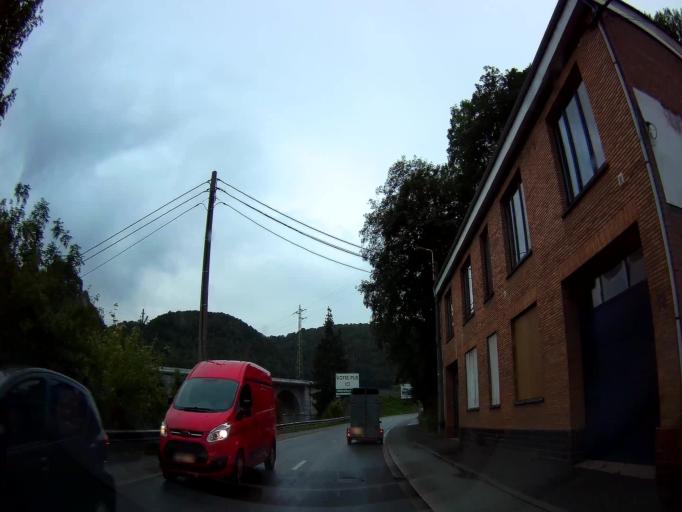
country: BE
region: Wallonia
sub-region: Province de Liege
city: Pepinster
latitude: 50.5747
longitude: 5.8305
